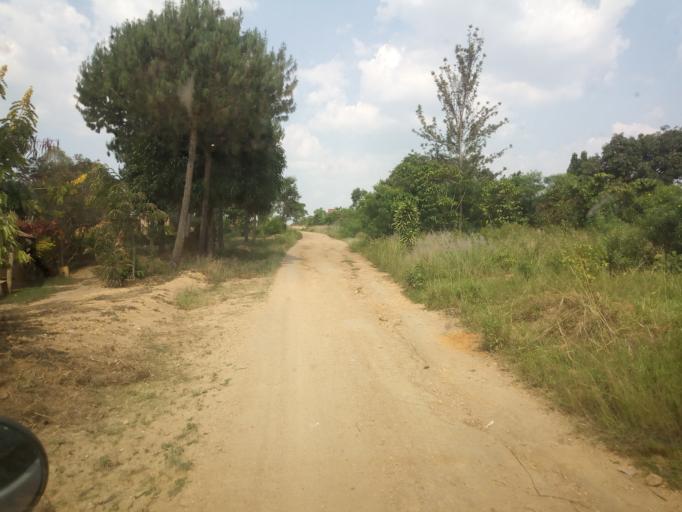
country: UG
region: Western Region
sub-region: Kanungu District
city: Ntungamo
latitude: -0.7901
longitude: 29.6573
